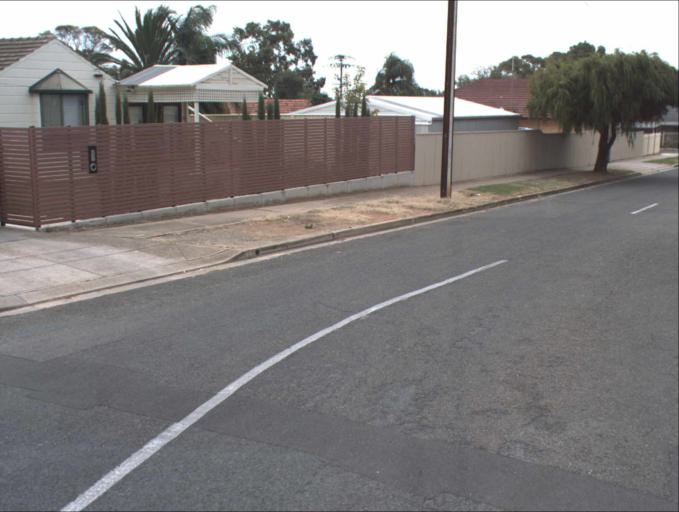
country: AU
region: South Australia
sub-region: Port Adelaide Enfield
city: Enfield
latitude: -34.8547
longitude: 138.6032
